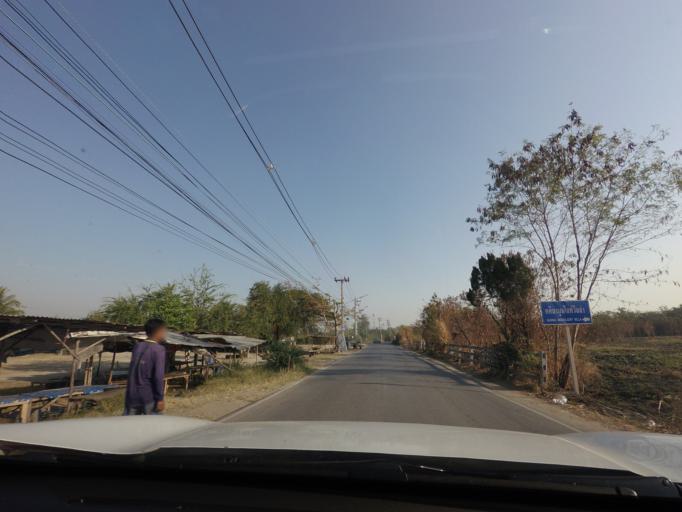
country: TH
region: Nakhon Ratchasima
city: Pak Chong
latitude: 14.6046
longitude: 101.4444
